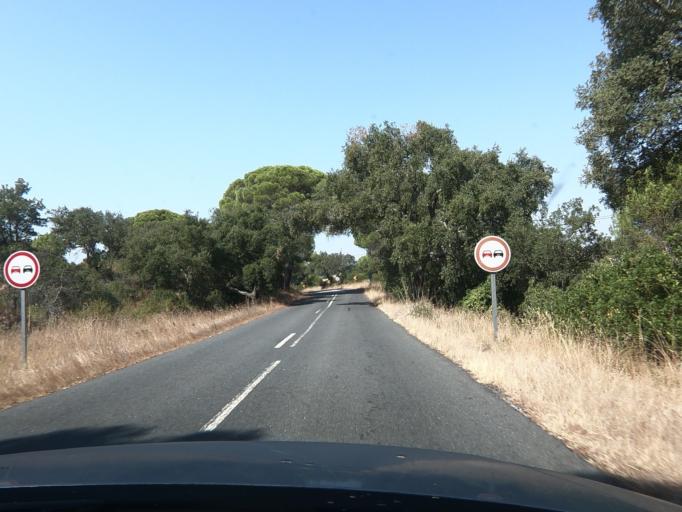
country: PT
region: Setubal
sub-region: Alcacer do Sal
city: Alcacer do Sal
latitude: 38.3057
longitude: -8.4205
